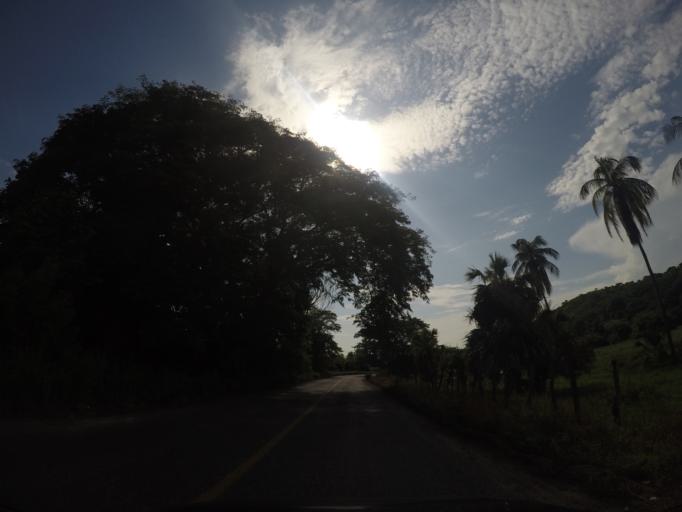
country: MX
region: Oaxaca
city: San Pedro Mixtepec
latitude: 15.9398
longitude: -97.1714
